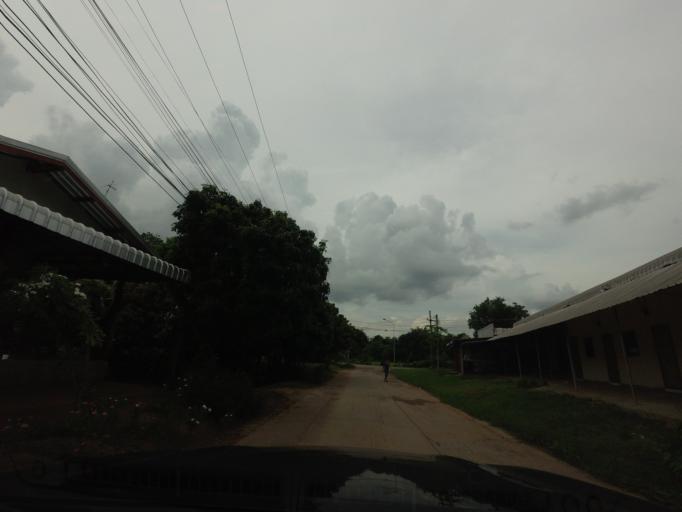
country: TH
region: Changwat Nong Bua Lamphu
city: Nong Bua Lamphu
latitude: 17.2726
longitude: 102.3925
